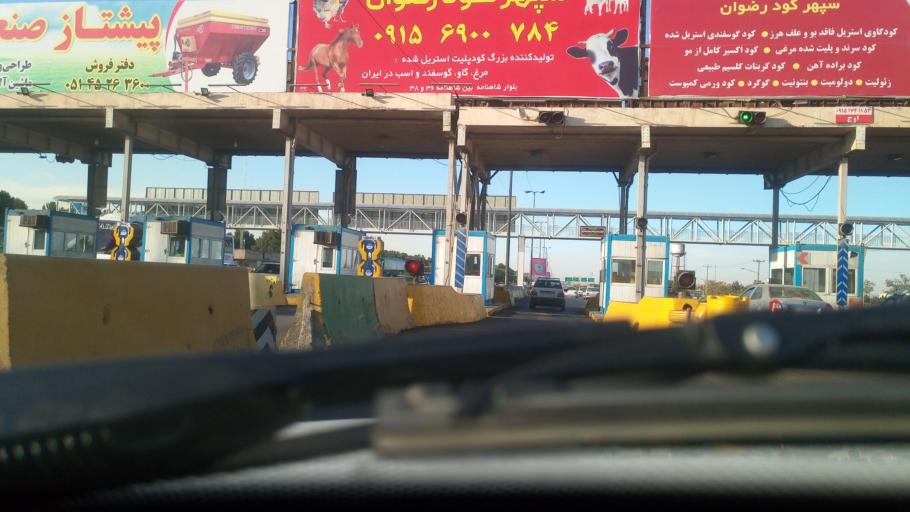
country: IR
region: Razavi Khorasan
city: Mashhad
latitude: 36.2179
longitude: 59.6258
